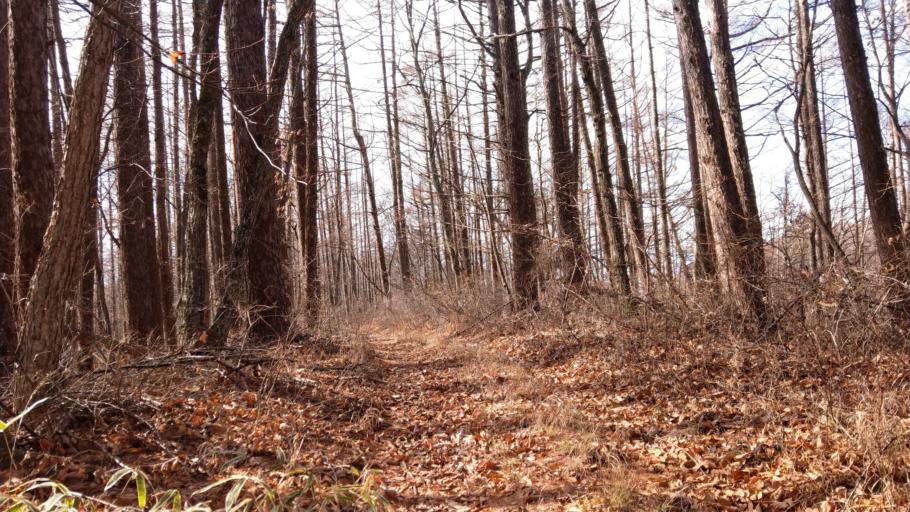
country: JP
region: Nagano
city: Komoro
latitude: 36.3783
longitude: 138.4351
